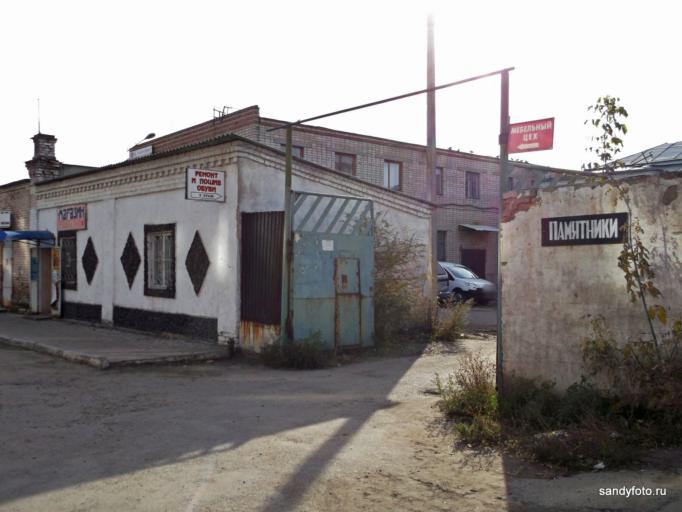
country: RU
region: Chelyabinsk
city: Troitsk
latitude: 54.0792
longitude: 61.5585
